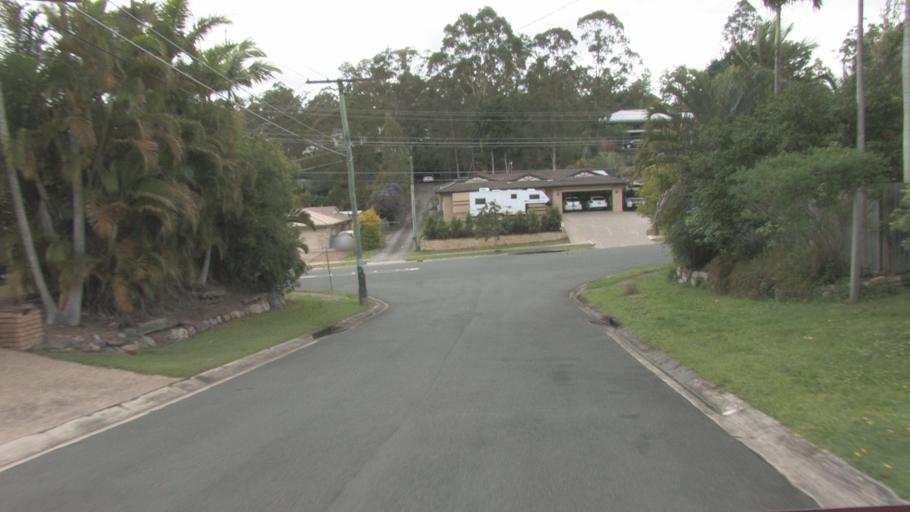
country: AU
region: Queensland
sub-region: Logan
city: Slacks Creek
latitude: -27.6531
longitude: 153.1862
